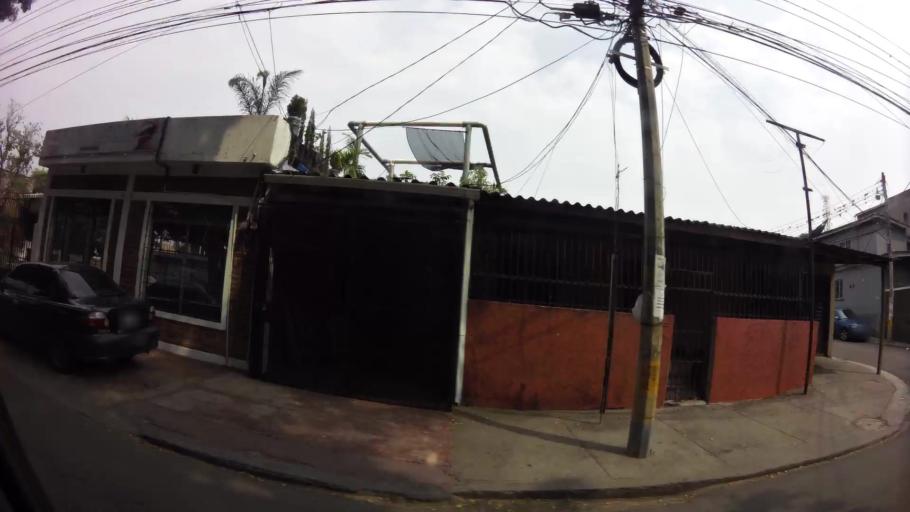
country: HN
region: Francisco Morazan
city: Tegucigalpa
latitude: 14.0730
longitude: -87.1889
